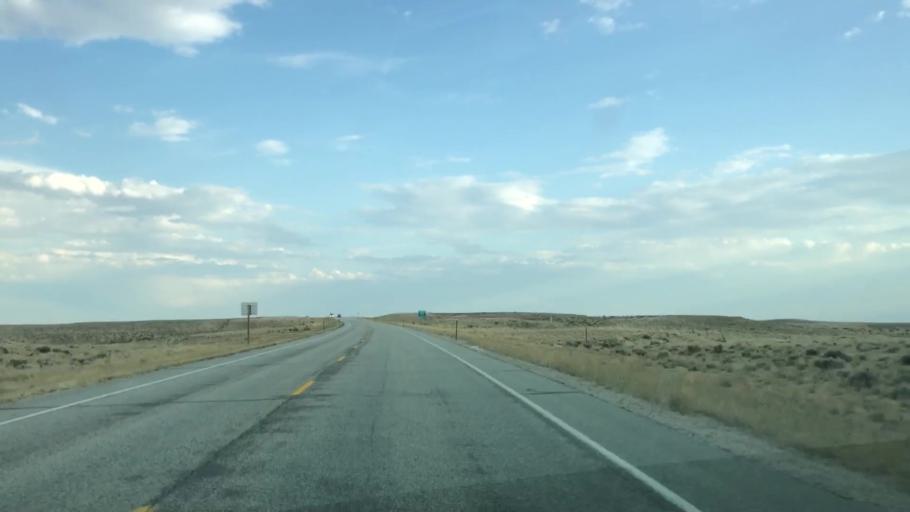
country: US
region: Wyoming
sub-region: Sweetwater County
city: North Rock Springs
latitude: 42.2811
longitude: -109.4859
